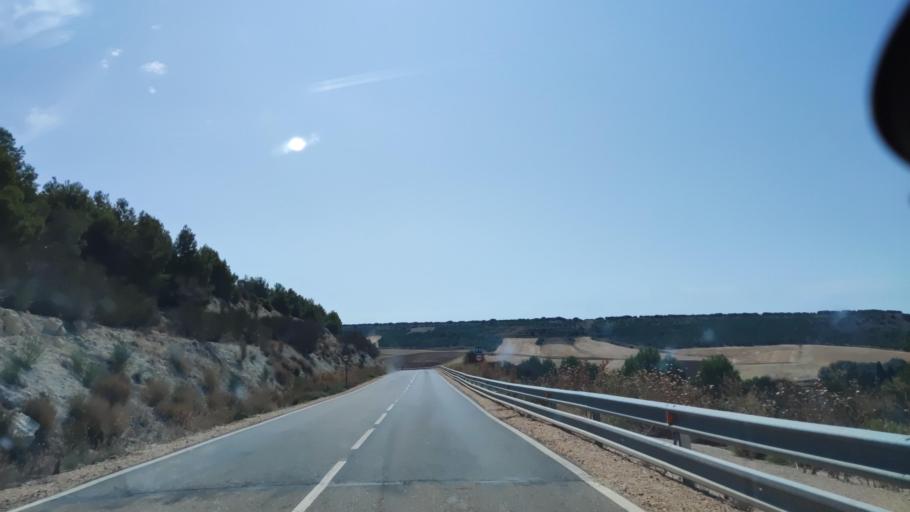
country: ES
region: Castille and Leon
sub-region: Provincia de Valladolid
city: Uruena
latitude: 41.7245
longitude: -5.1976
